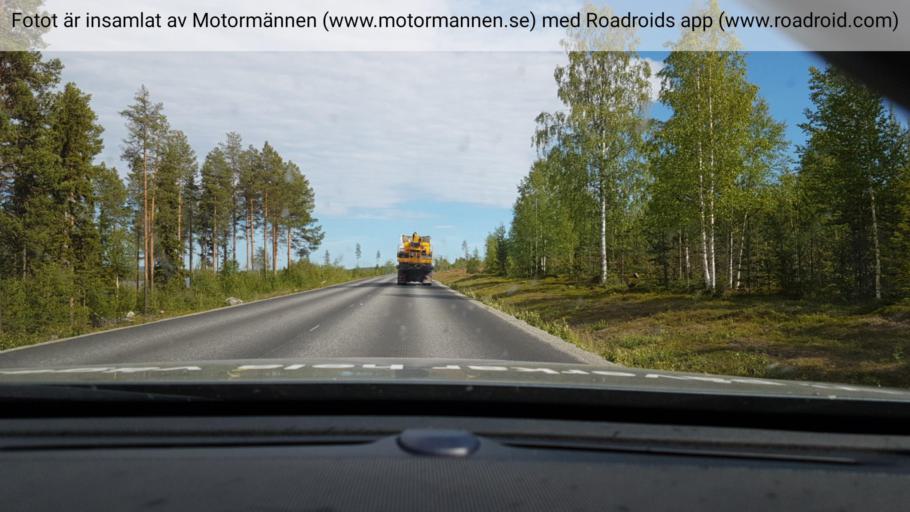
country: SE
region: Vaesterbotten
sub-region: Lycksele Kommun
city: Soderfors
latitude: 64.8386
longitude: 17.9870
